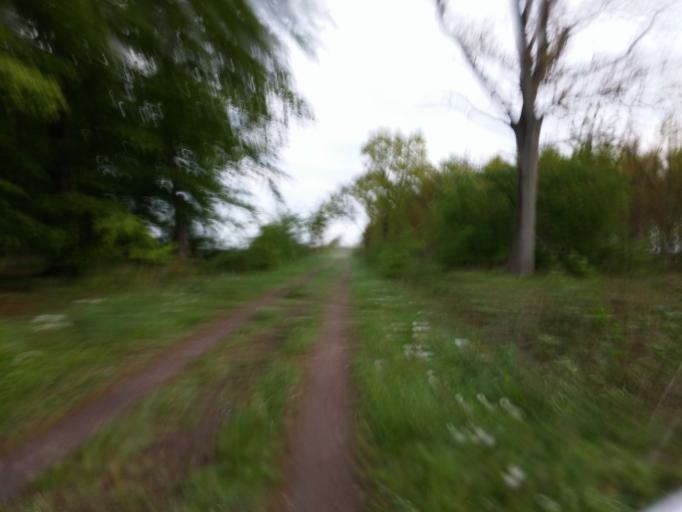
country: DK
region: South Denmark
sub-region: Kerteminde Kommune
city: Munkebo
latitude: 55.4283
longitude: 10.5484
